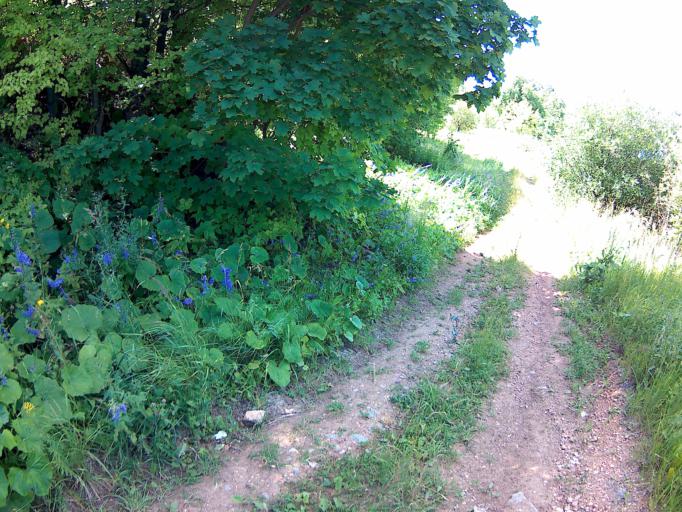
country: RU
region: Nizjnij Novgorod
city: Nizhniy Novgorod
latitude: 56.2381
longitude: 43.9372
